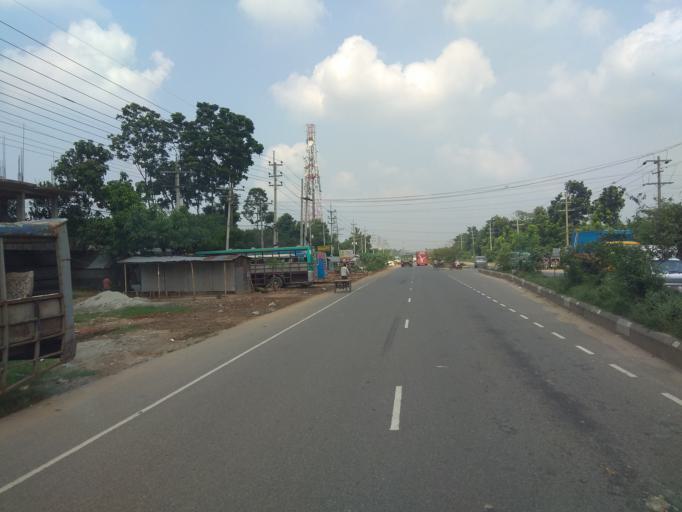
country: BD
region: Dhaka
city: Gafargaon
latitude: 24.1789
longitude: 90.4272
